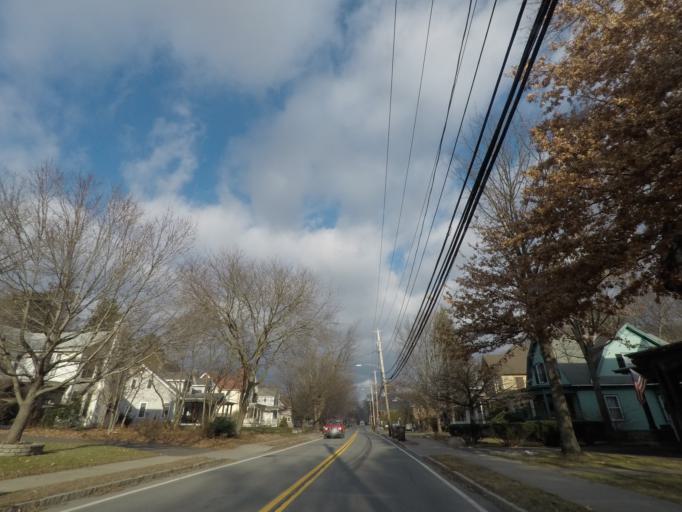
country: US
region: New York
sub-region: Albany County
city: Voorheesville
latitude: 42.6506
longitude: -73.9297
